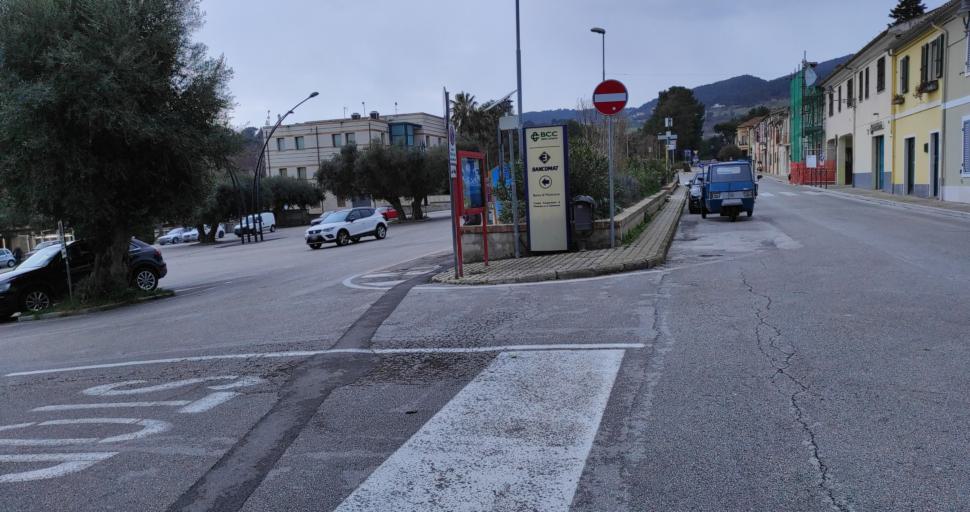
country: IT
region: The Marches
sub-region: Provincia di Ancona
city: Sirolo
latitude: 43.5256
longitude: 13.6171
